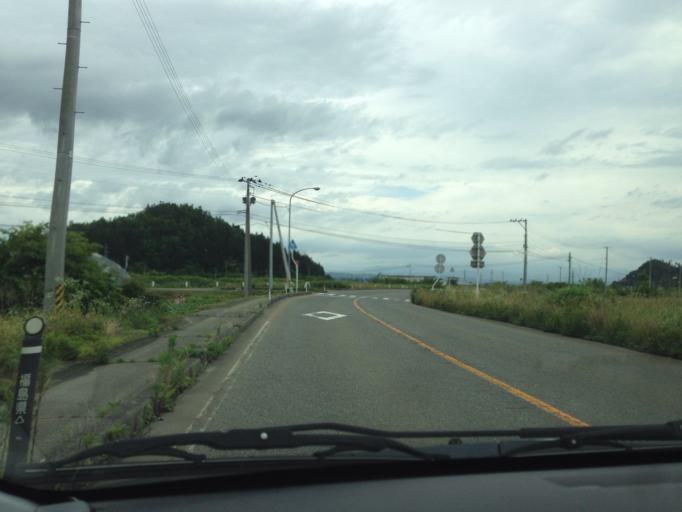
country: JP
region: Fukushima
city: Kitakata
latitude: 37.4310
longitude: 139.8824
